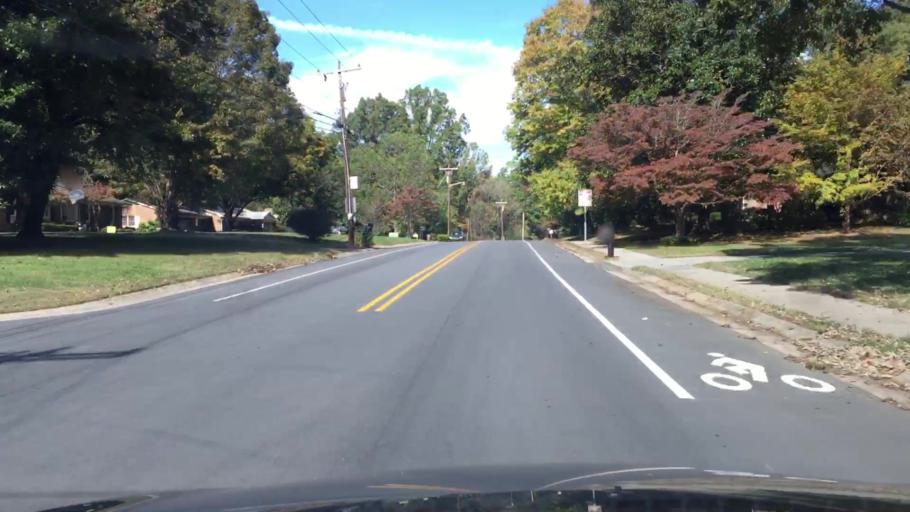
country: US
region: North Carolina
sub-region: Iredell County
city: Mooresville
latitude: 35.5657
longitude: -80.8029
